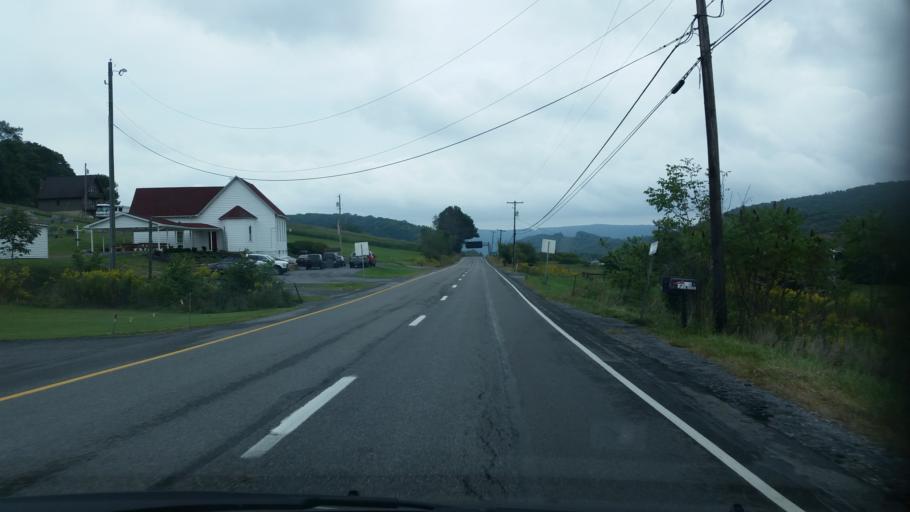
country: US
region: Pennsylvania
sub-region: Centre County
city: Stormstown
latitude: 40.8194
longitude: -78.0970
